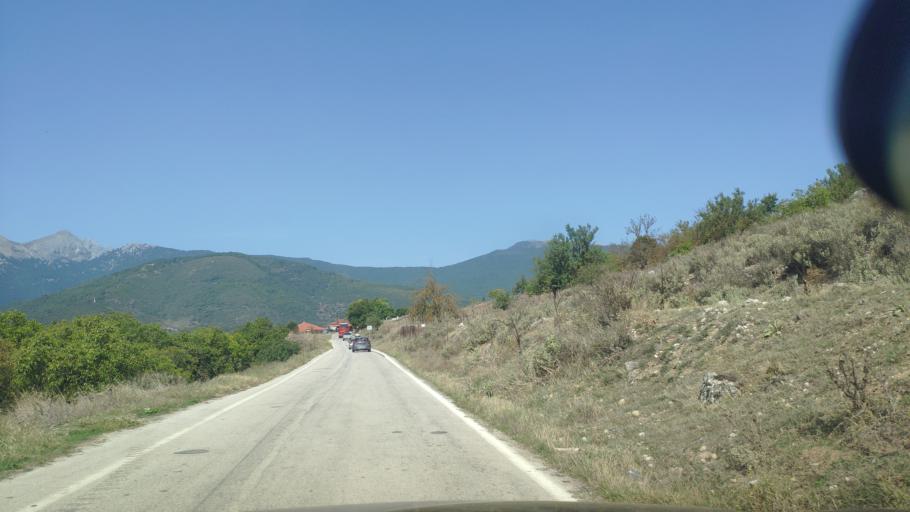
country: GR
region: West Greece
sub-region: Nomos Achaias
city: Aiyira
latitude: 37.9013
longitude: 22.3335
